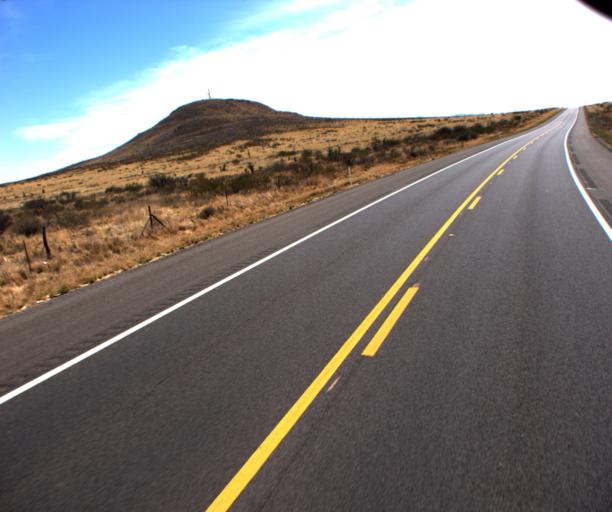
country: US
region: Arizona
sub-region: Cochise County
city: Willcox
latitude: 31.9049
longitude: -109.7190
